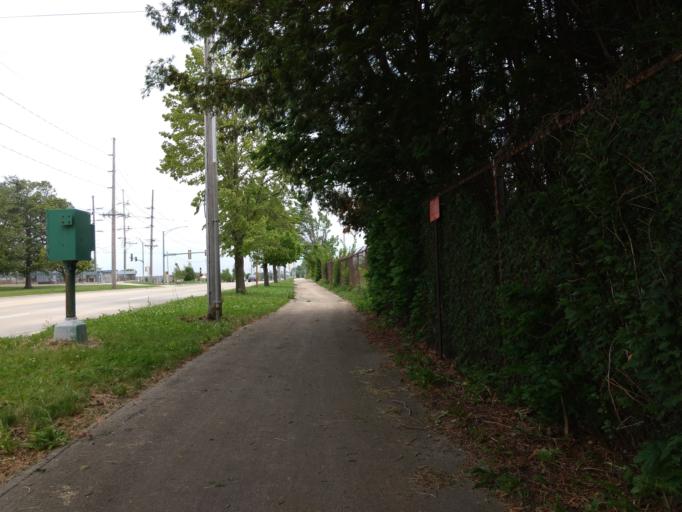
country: US
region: Illinois
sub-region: Champaign County
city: Urbana
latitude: 40.0836
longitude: -88.1922
